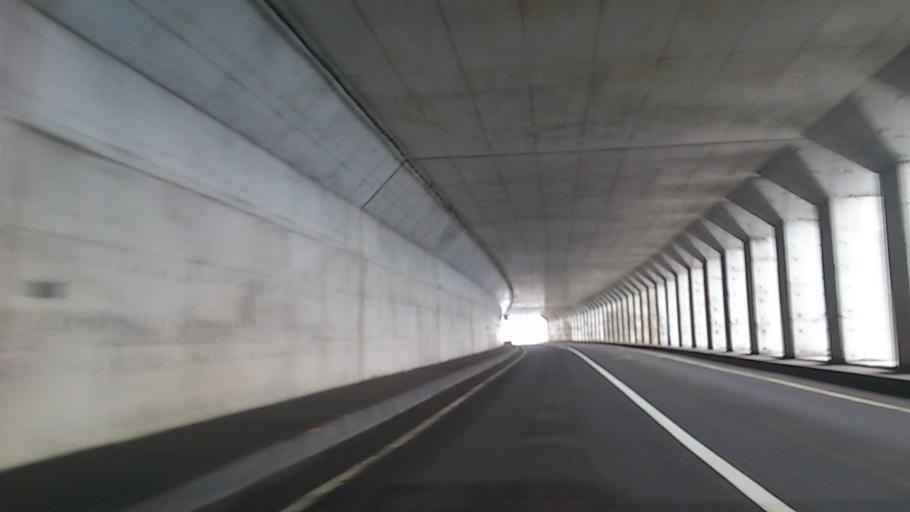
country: JP
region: Hokkaido
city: Iwanai
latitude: 42.6881
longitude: 139.9309
